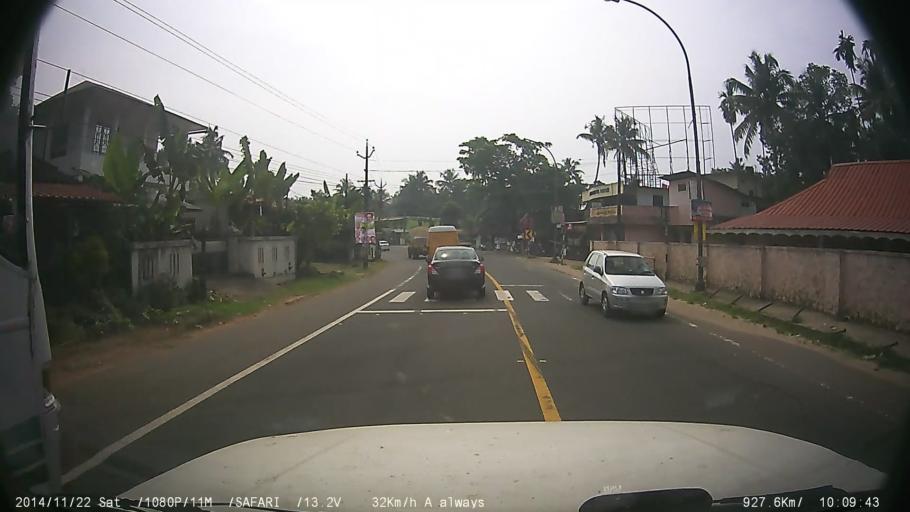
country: IN
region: Kerala
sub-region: Ernakulam
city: Muvattupula
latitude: 10.0296
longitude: 76.5491
